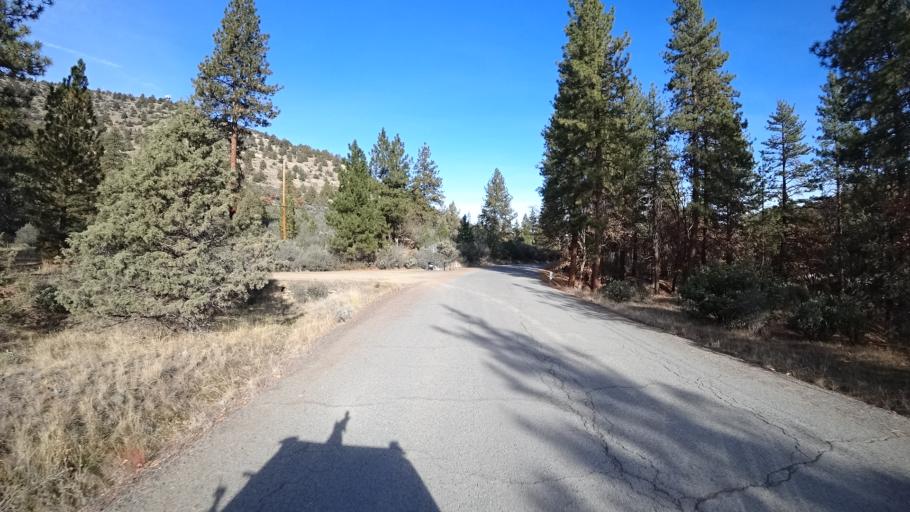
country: US
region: California
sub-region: Siskiyou County
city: Montague
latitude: 41.6020
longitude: -122.5779
